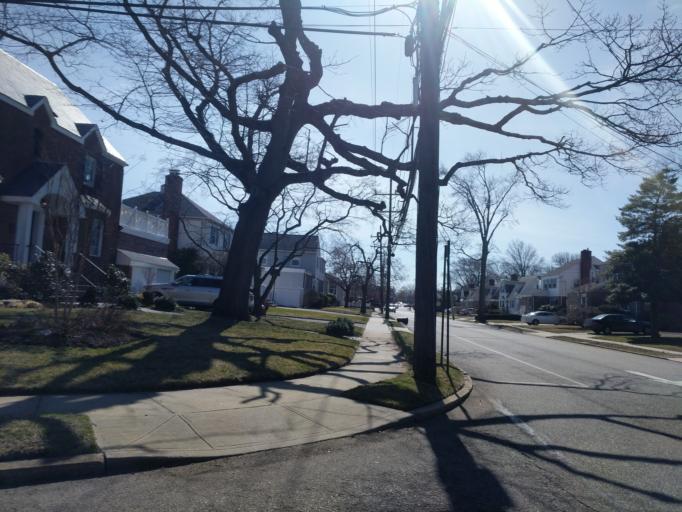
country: US
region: New York
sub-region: Nassau County
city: Lynbrook
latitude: 40.6548
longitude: -73.6828
